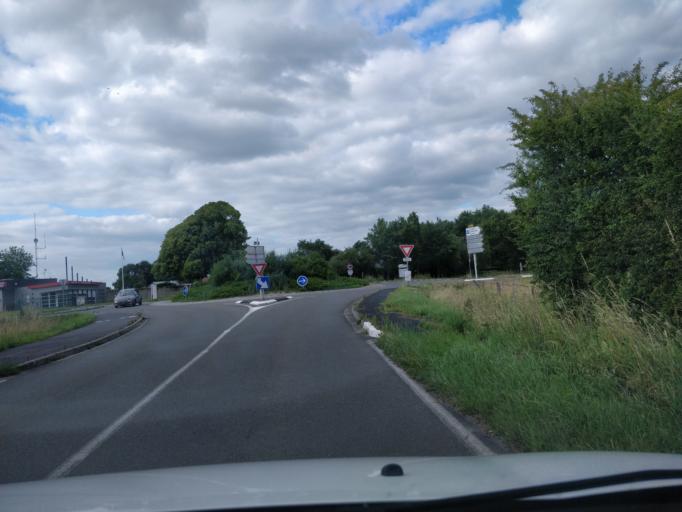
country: FR
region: Pays de la Loire
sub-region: Departement de Maine-et-Loire
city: Feneu
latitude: 47.5648
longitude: -0.5968
